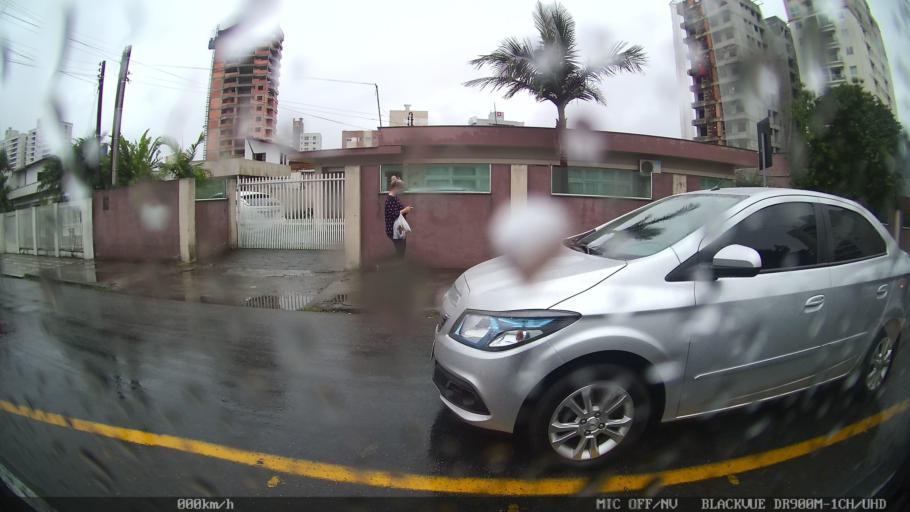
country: BR
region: Santa Catarina
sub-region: Itajai
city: Itajai
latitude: -26.9098
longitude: -48.6774
